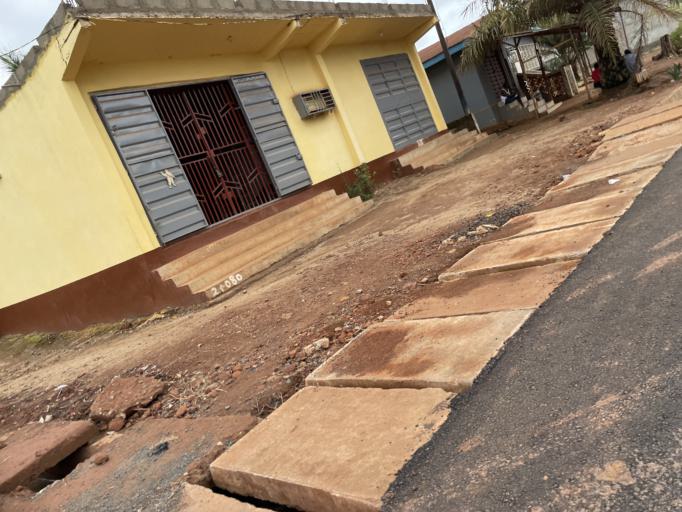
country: SL
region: Western Area
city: Hastings
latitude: 8.4035
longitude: -13.1441
